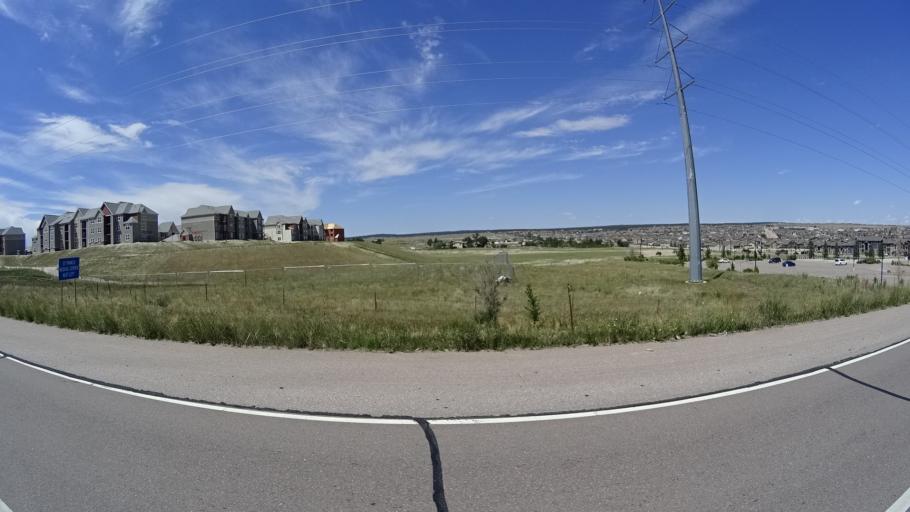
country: US
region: Colorado
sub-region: El Paso County
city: Black Forest
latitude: 38.9409
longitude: -104.7033
